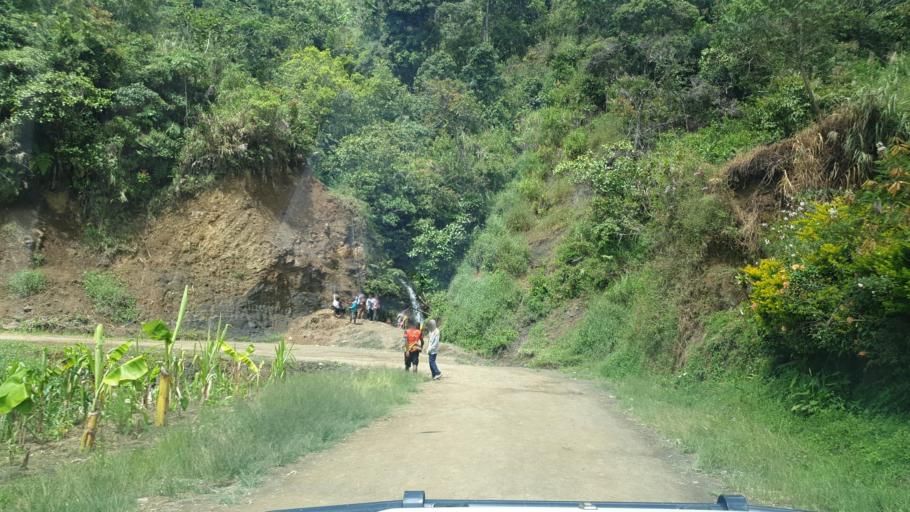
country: PG
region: Eastern Highlands
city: Goroka
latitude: -6.2781
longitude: 145.1858
